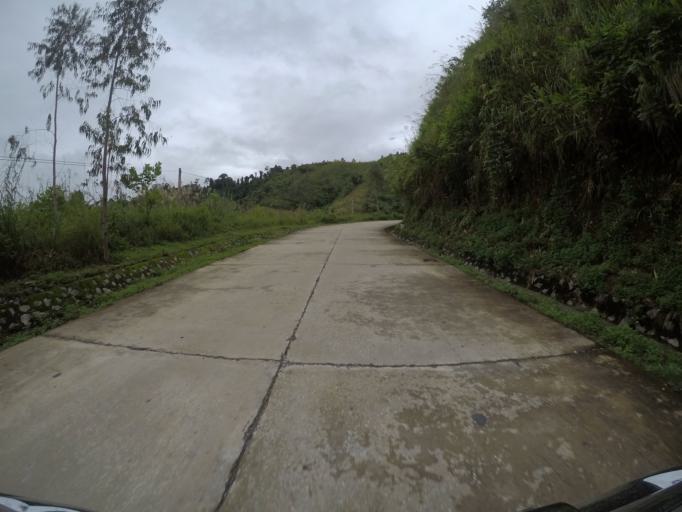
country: VN
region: Quang Nam
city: Thanh My
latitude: 15.6542
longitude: 107.6688
